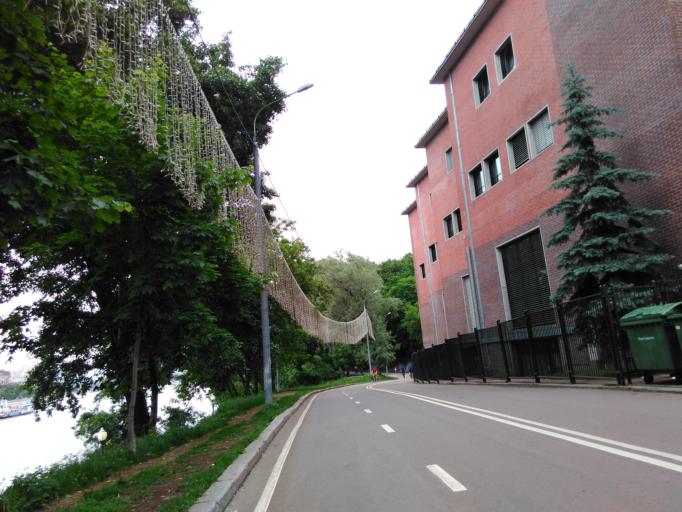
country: RU
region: Moscow
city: Novyye Cheremushki
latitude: 55.7147
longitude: 37.5808
